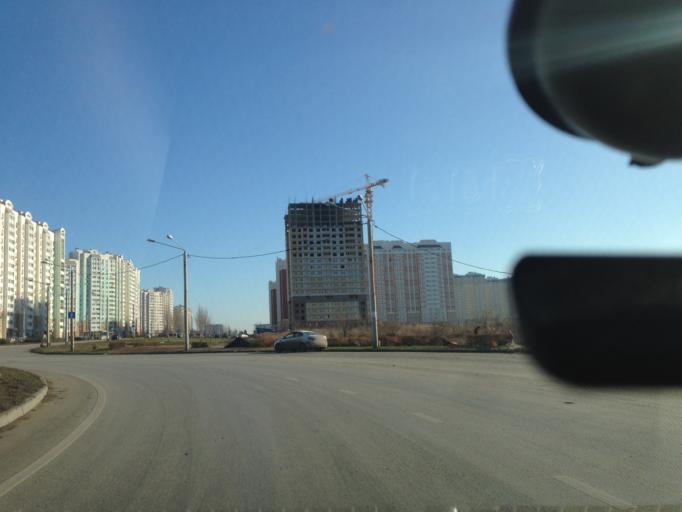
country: RU
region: Rostov
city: Kalinin
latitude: 47.2320
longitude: 39.5894
